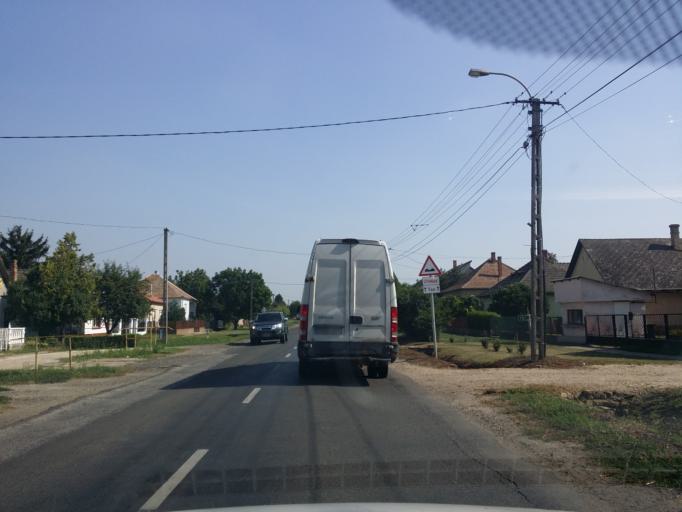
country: HU
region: Fejer
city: Mezofalva
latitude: 46.9287
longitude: 18.7859
